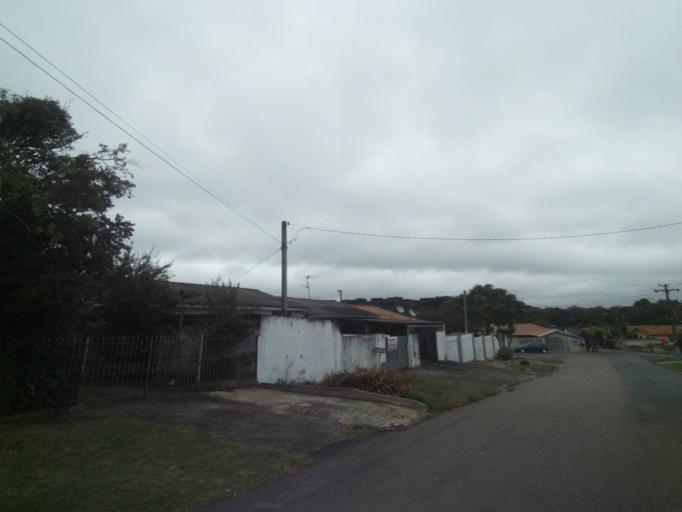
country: BR
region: Parana
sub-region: Curitiba
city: Curitiba
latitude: -25.5174
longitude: -49.3108
